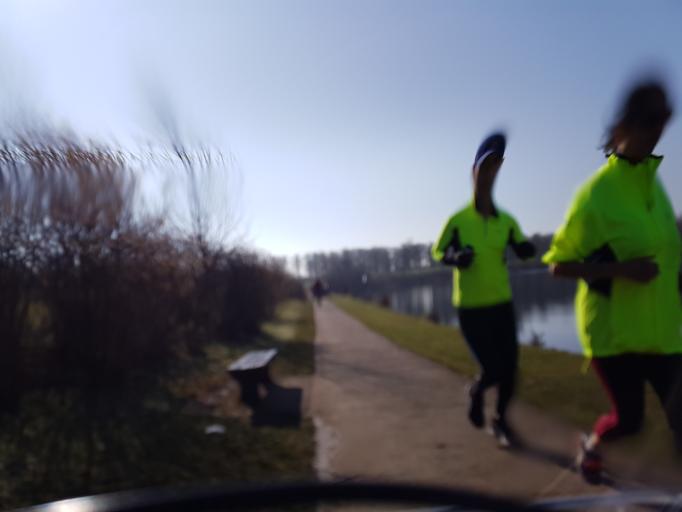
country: GB
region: England
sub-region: Milton Keynes
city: Broughton
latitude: 52.0501
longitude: -0.7138
